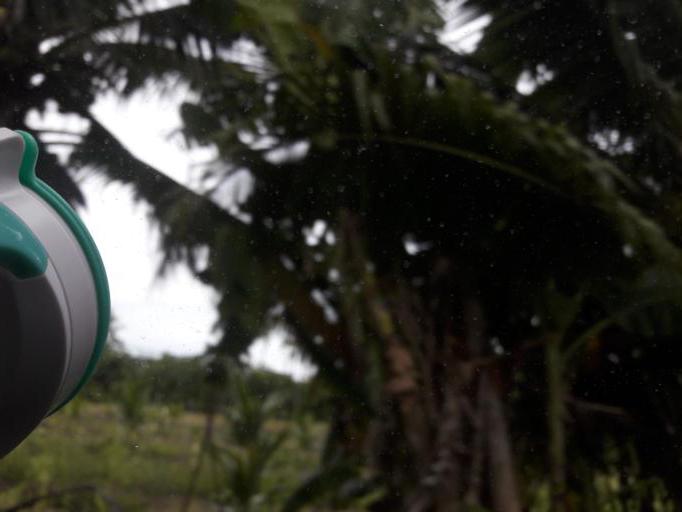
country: TH
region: Ratchaburi
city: Damnoen Saduak
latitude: 13.5375
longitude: 100.0051
